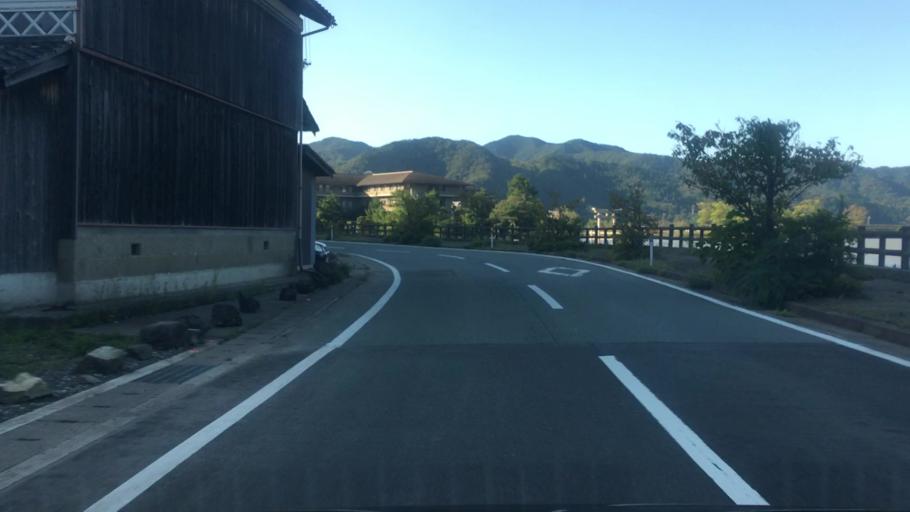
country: JP
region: Hyogo
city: Toyooka
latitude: 35.6186
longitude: 134.8214
